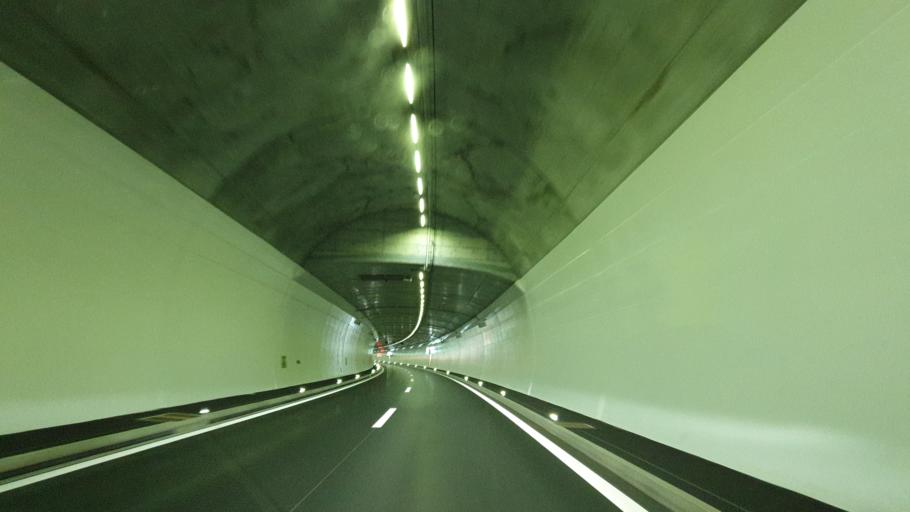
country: CH
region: Valais
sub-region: Visp District
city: Visp
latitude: 46.2957
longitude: 7.9237
